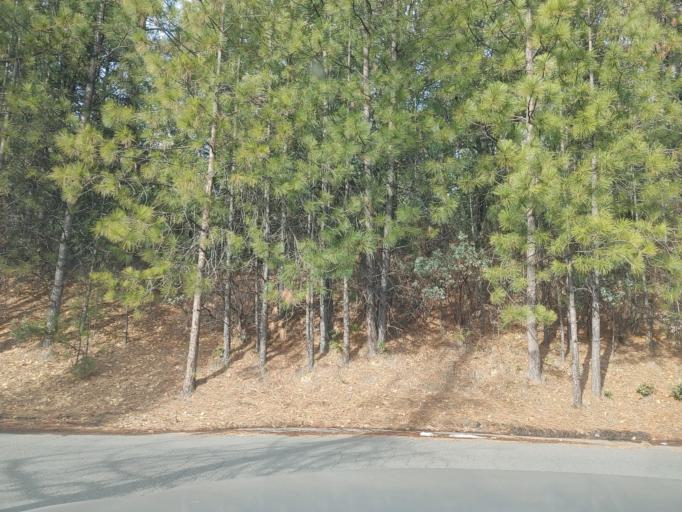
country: US
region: California
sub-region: Tuolumne County
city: Twain Harte
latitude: 38.0408
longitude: -120.2251
